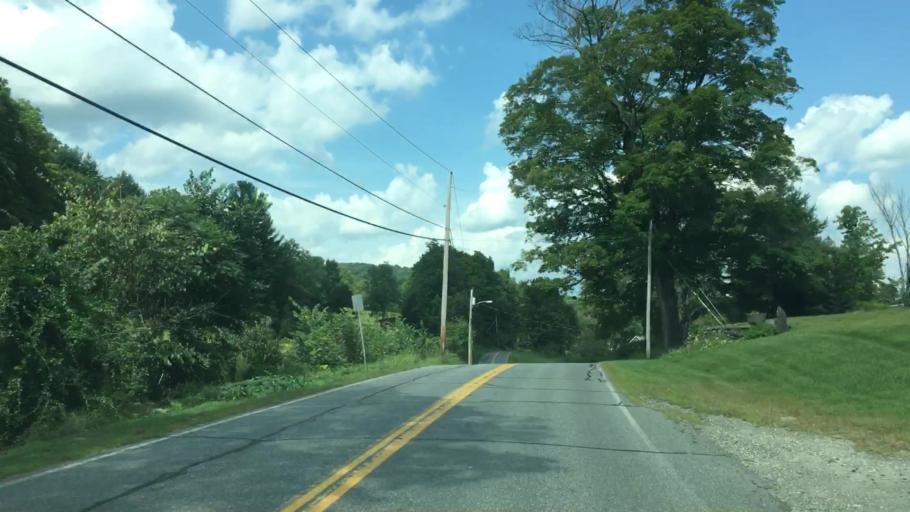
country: US
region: Vermont
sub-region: Windham County
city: West Brattleboro
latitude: 42.7944
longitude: -72.5984
